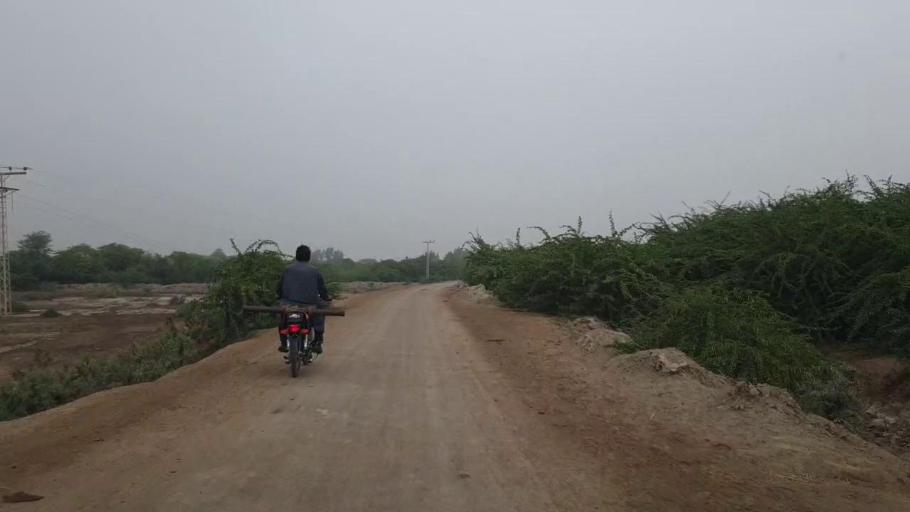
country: PK
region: Sindh
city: Badin
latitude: 24.5847
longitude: 68.6666
